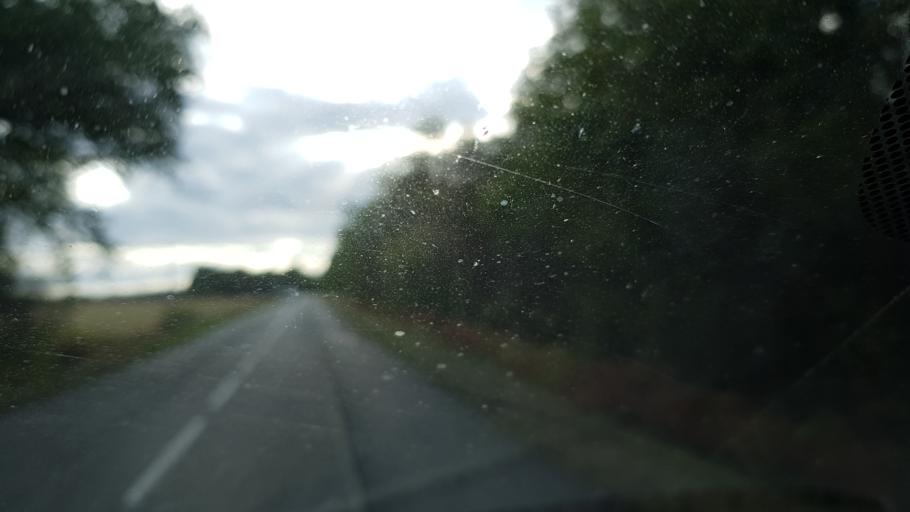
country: FR
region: Centre
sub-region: Departement du Loiret
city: Saint-Pere-sur-Loire
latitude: 47.7069
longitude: 2.3245
